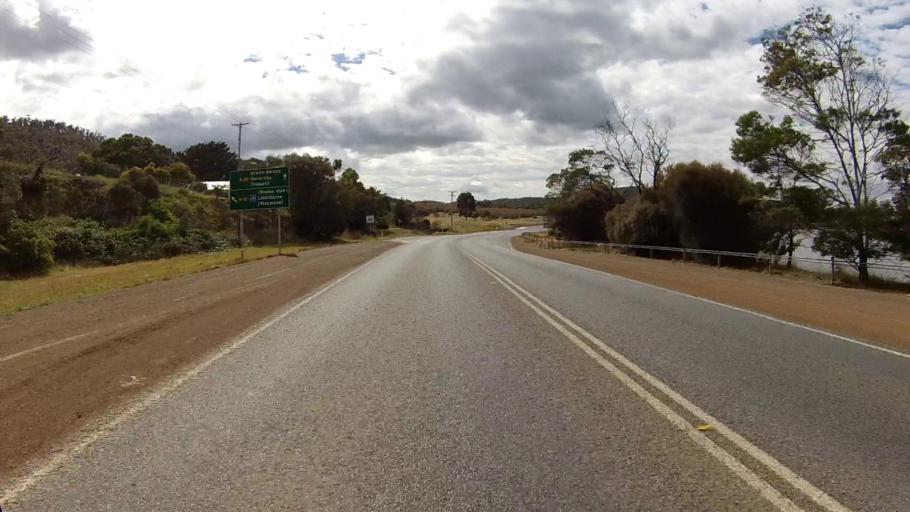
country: AU
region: Tasmania
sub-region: Glenorchy
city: Goodwood
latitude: -42.8117
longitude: 147.3060
